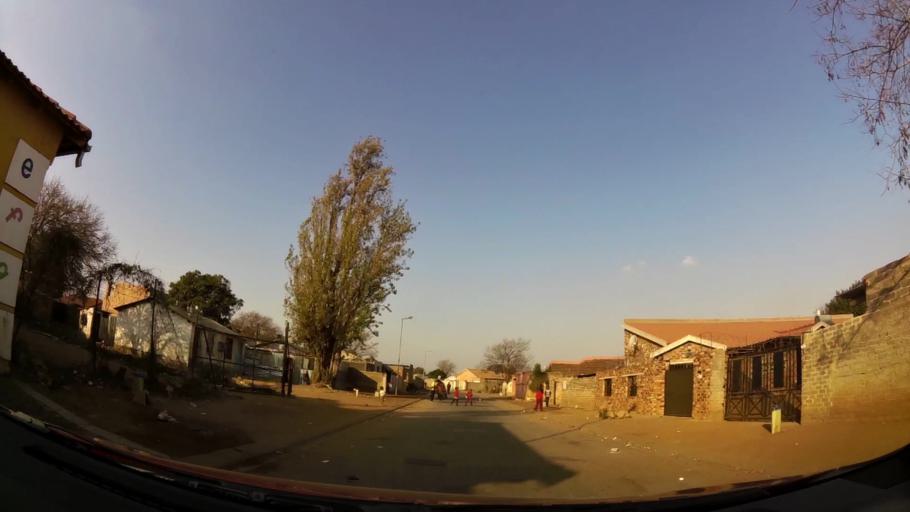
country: ZA
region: Gauteng
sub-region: City of Johannesburg Metropolitan Municipality
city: Soweto
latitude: -26.2932
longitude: 27.8938
